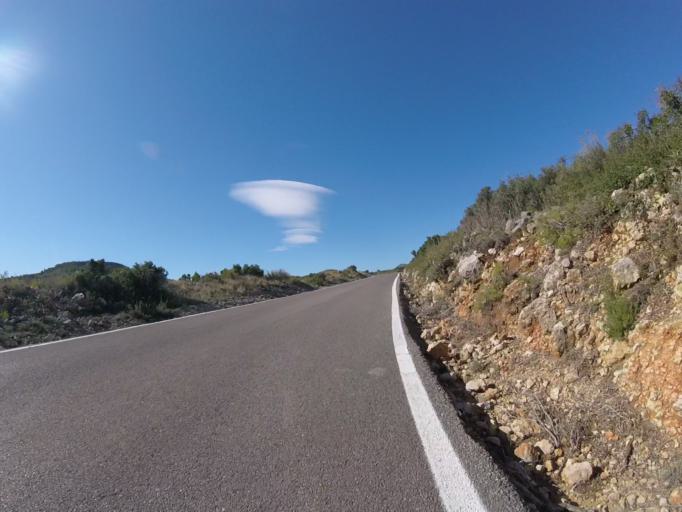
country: ES
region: Valencia
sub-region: Provincia de Castello
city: Albocasser
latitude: 40.3922
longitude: 0.0400
